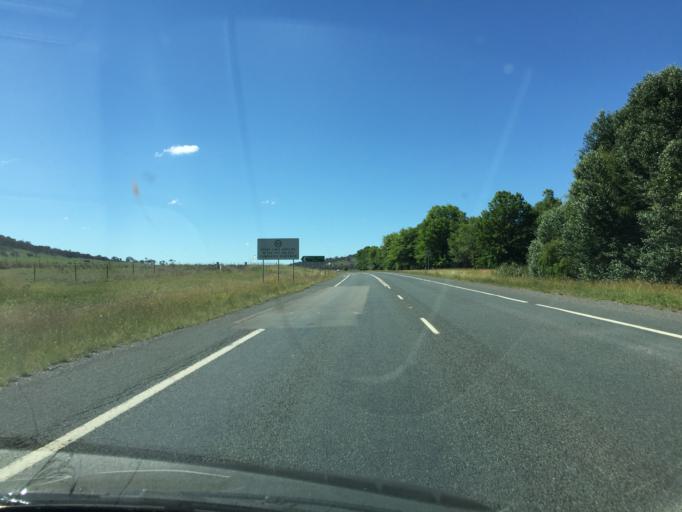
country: AU
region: Australian Capital Territory
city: Macarthur
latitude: -35.4917
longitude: 149.1504
